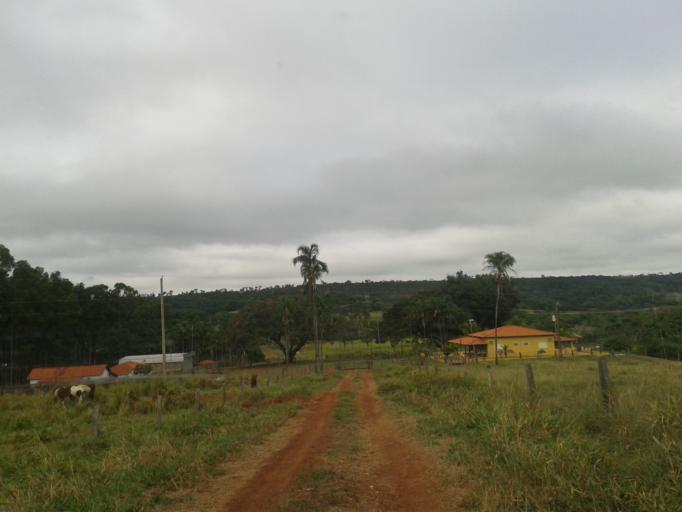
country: BR
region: Minas Gerais
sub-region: Campina Verde
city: Campina Verde
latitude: -19.4260
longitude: -49.6473
